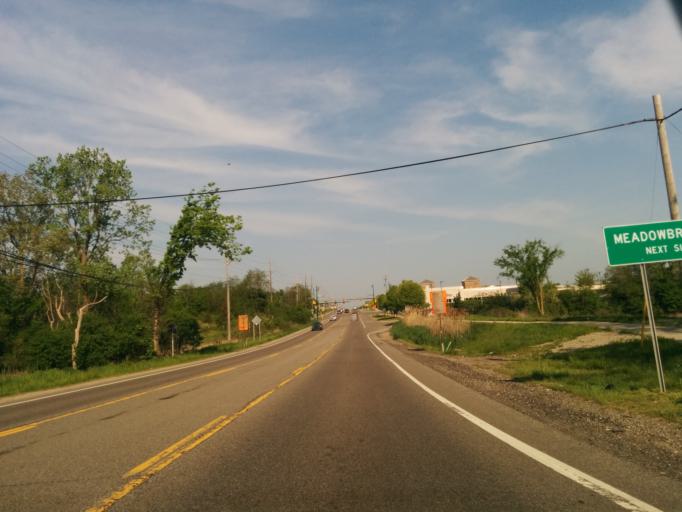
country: US
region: Michigan
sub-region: Oakland County
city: Novi
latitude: 42.4757
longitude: -83.4524
